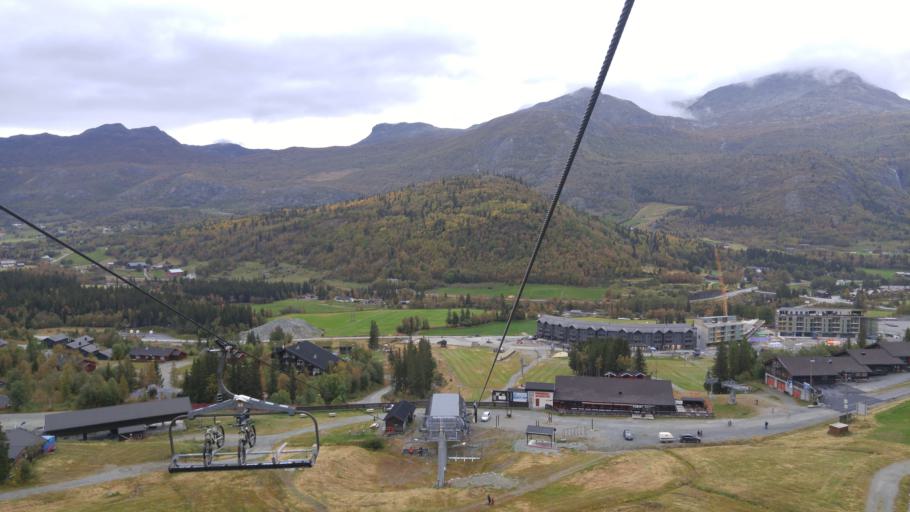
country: NO
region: Buskerud
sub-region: Hemsedal
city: Hemsedal
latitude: 60.8586
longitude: 8.5132
